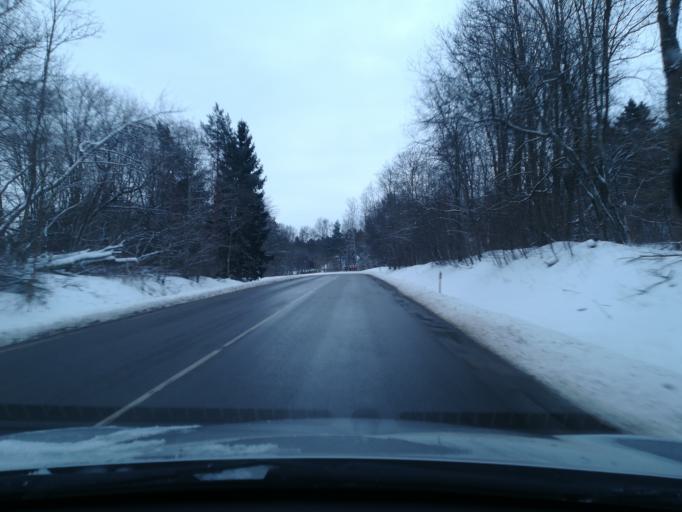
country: EE
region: Harju
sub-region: Keila linn
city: Keila
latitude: 59.4158
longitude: 24.3400
